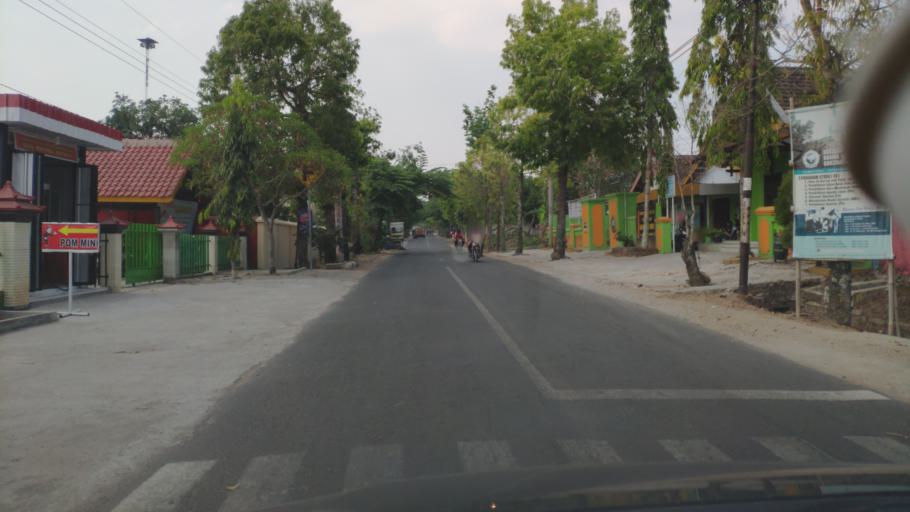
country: ID
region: Central Java
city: Kunden
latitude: -6.9613
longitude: 111.4134
